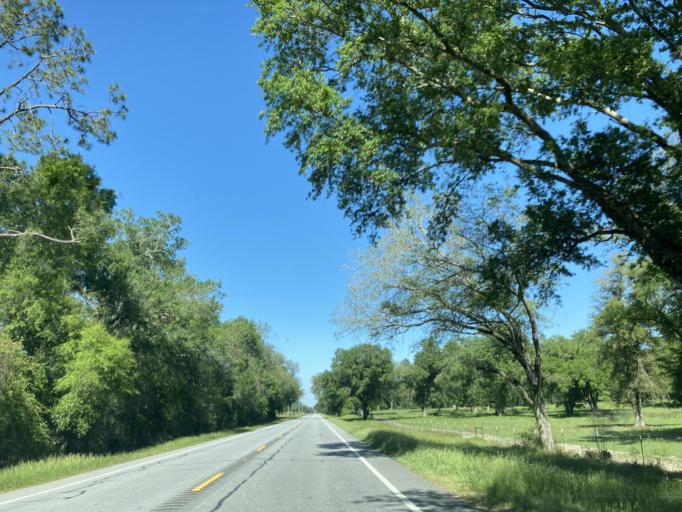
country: US
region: Georgia
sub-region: Baker County
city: Newton
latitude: 31.2571
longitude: -84.4147
